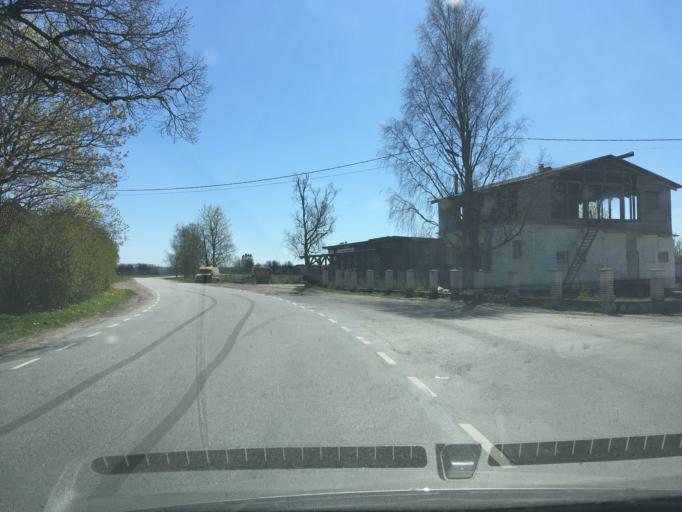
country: EE
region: Harju
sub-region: Raasiku vald
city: Raasiku
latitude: 59.3361
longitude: 25.1536
